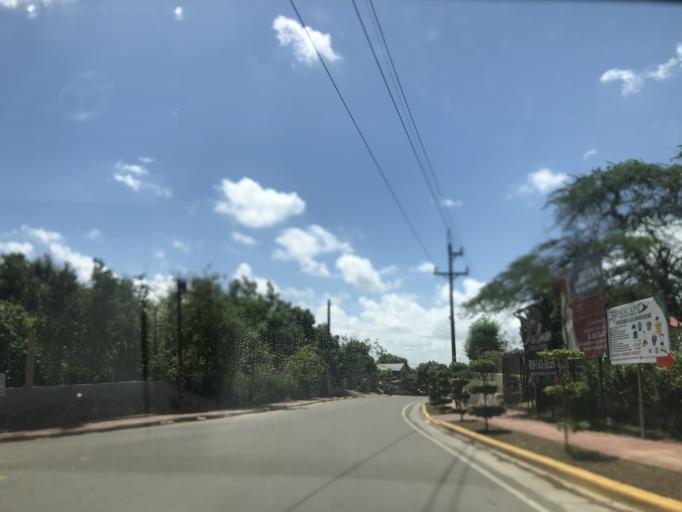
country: DO
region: Santiago
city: La Canela
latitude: 19.4517
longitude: -70.7691
